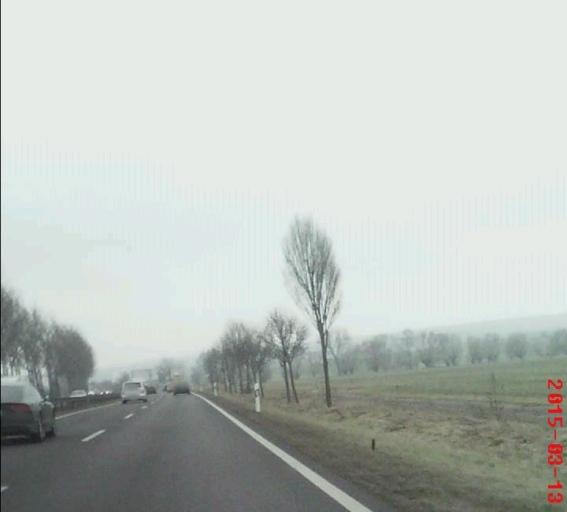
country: DE
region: Thuringia
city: Walschleben
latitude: 51.0579
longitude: 10.9324
